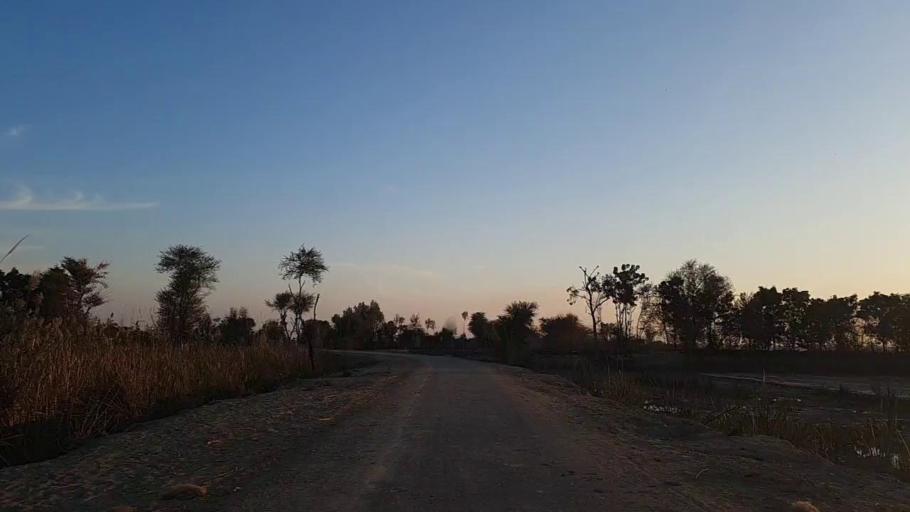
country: PK
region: Sindh
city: Bandhi
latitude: 26.6278
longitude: 68.3706
